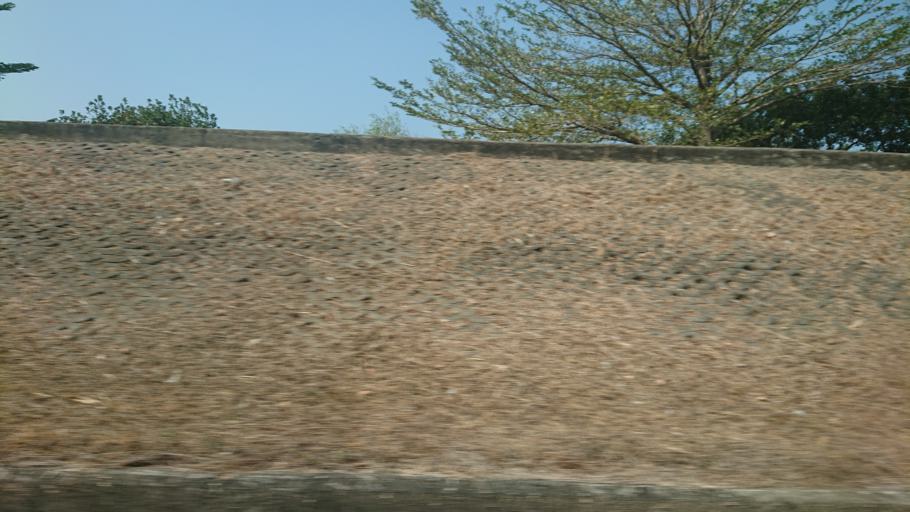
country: TW
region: Taiwan
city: Lugu
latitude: 23.7571
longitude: 120.6591
